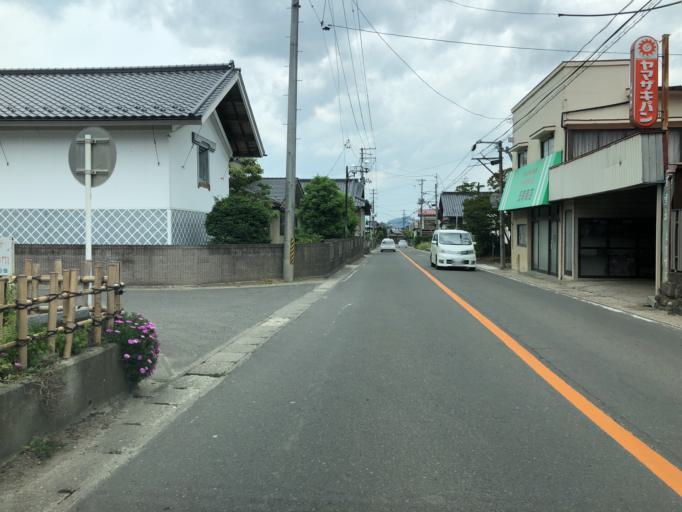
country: JP
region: Miyagi
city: Marumori
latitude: 37.8663
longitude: 140.8269
